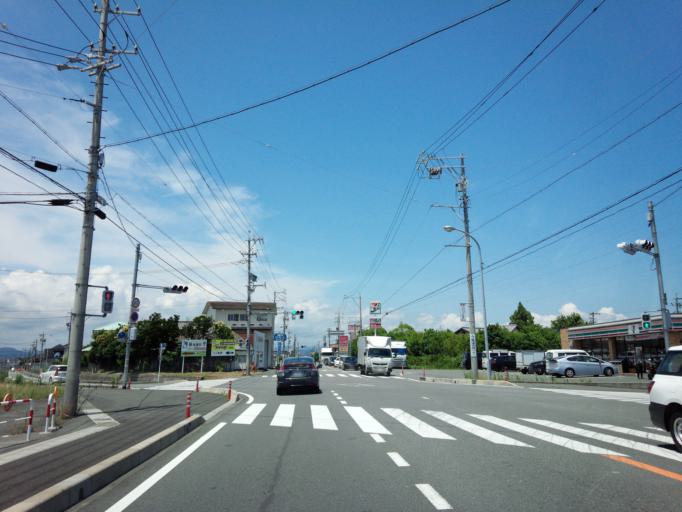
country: JP
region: Shizuoka
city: Shimada
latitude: 34.7844
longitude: 138.2545
